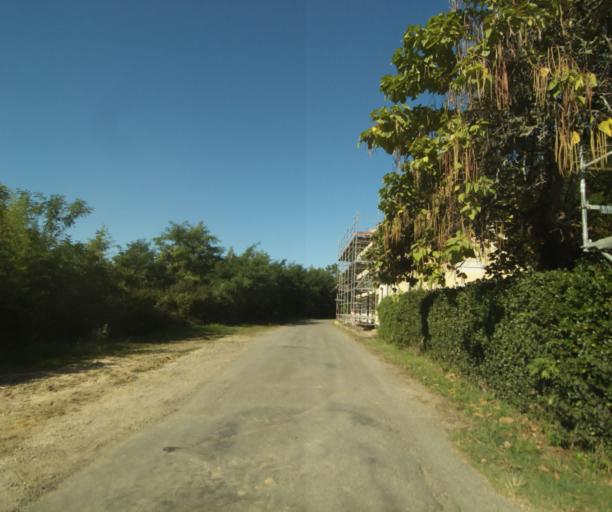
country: FR
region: Midi-Pyrenees
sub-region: Departement du Gers
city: Cazaubon
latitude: 43.9526
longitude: -0.0446
